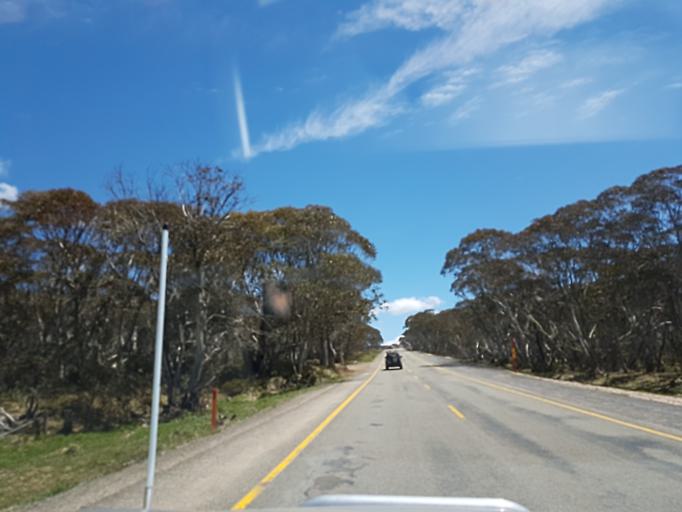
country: AU
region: Victoria
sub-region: Alpine
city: Mount Beauty
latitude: -37.0230
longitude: 147.2478
